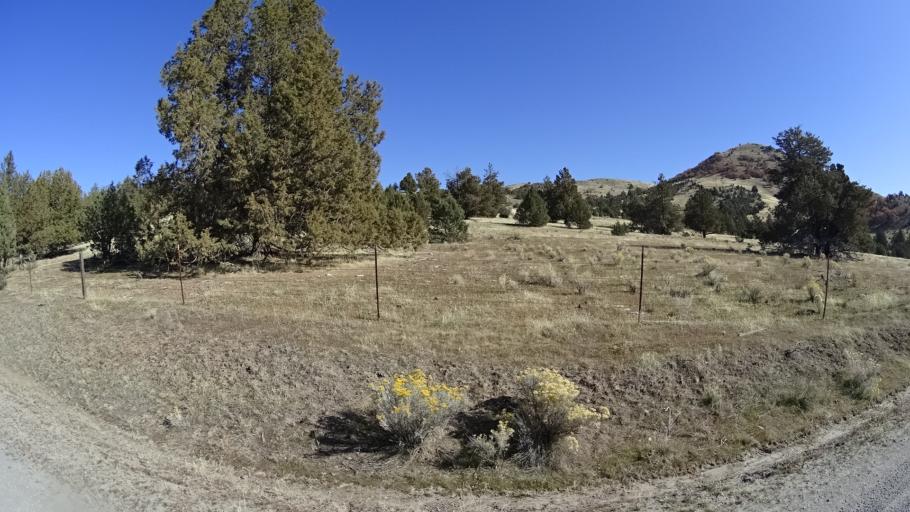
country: US
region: California
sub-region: Siskiyou County
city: Montague
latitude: 41.8030
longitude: -122.3702
